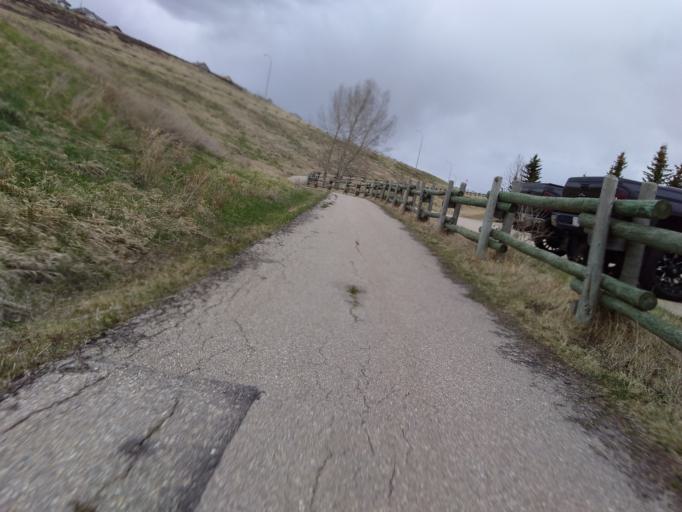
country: CA
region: Alberta
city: Cochrane
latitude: 51.1908
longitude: -114.4323
